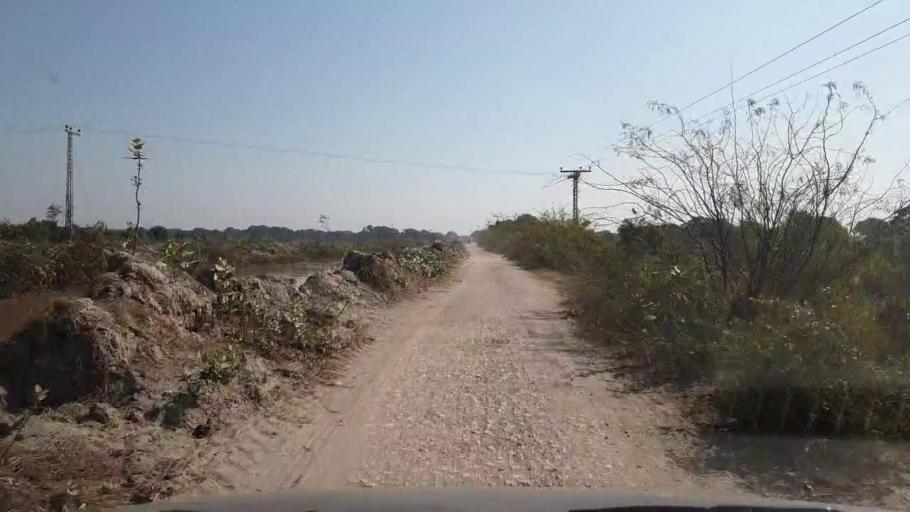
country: PK
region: Sindh
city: Tando Allahyar
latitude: 25.4493
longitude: 68.6275
